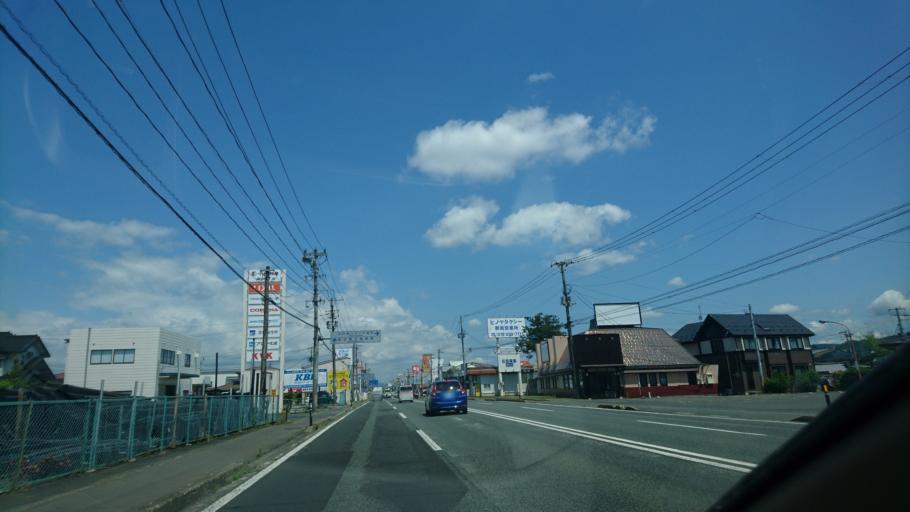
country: JP
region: Iwate
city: Morioka-shi
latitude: 39.6558
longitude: 141.1631
